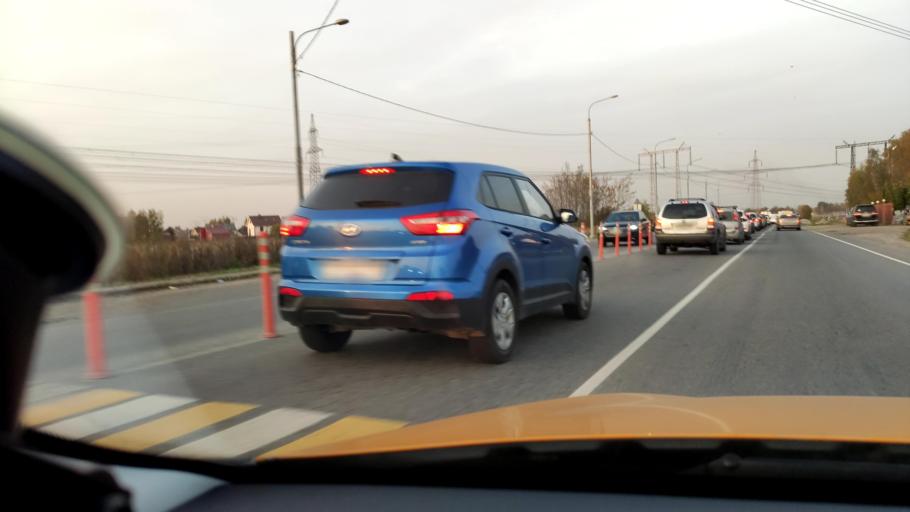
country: RU
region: Moskovskaya
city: Povedniki
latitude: 55.9566
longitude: 37.6524
